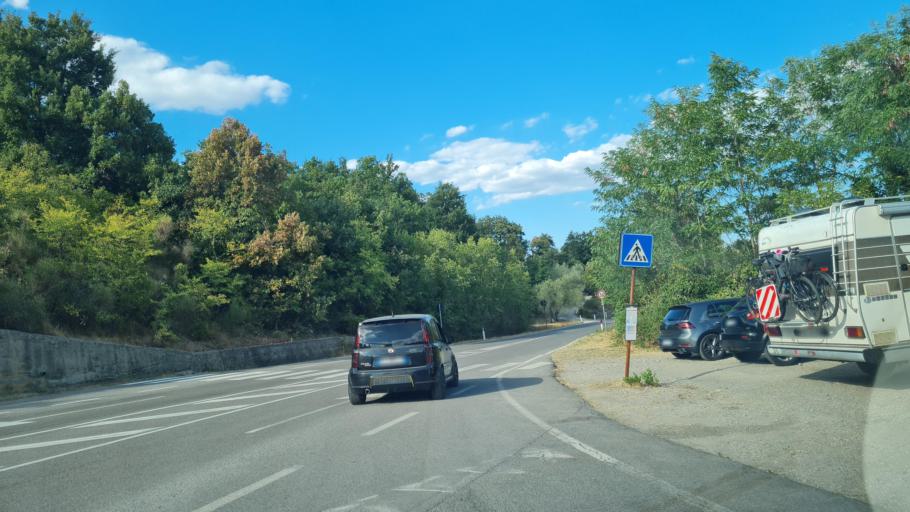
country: IT
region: Tuscany
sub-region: Provincia di Siena
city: Abbadia San Salvatore
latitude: 42.9312
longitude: 11.7000
